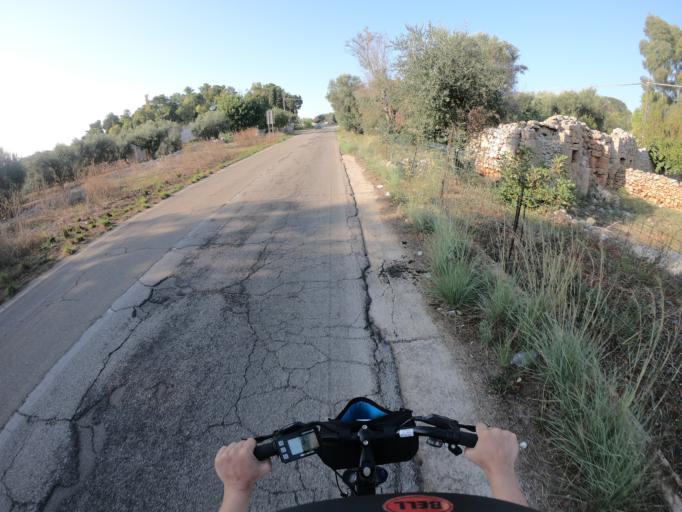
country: IT
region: Apulia
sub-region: Provincia di Lecce
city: Castrignano del Capo
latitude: 39.8179
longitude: 18.3564
